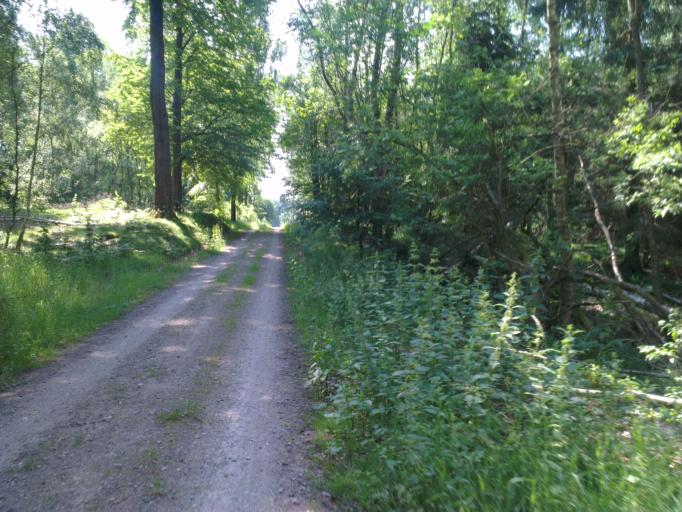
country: DK
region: Capital Region
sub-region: Allerod Kommune
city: Lillerod
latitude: 55.9148
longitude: 12.3588
